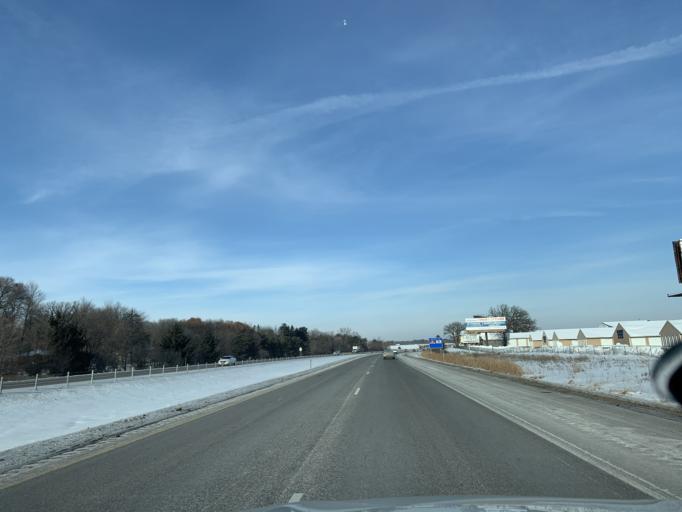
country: US
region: Minnesota
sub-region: Chisago County
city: Wyoming
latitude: 45.3286
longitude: -93.0041
